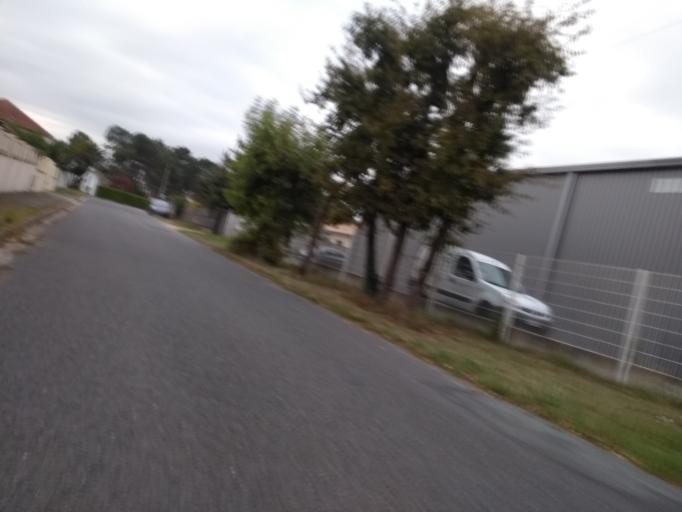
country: FR
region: Aquitaine
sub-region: Departement de la Gironde
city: Talence
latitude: 44.7828
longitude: -0.5920
